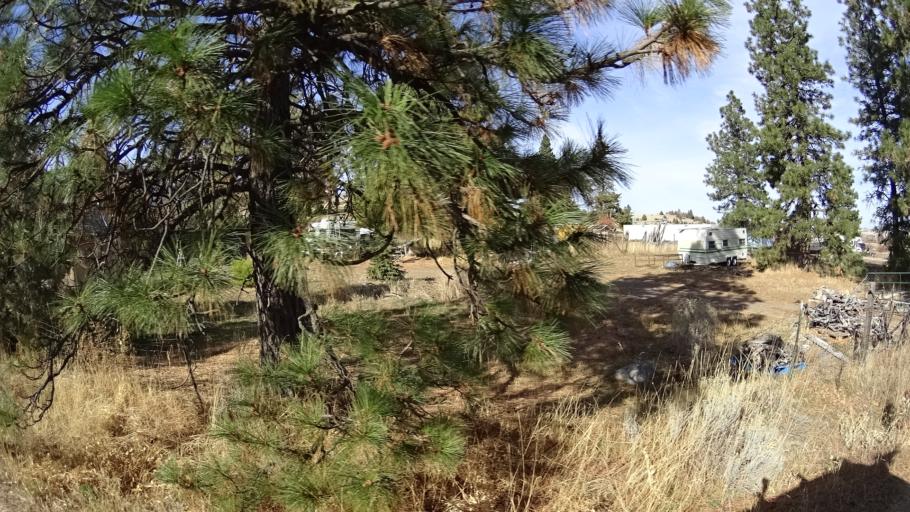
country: US
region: California
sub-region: Siskiyou County
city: Weed
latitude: 41.4456
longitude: -122.4340
